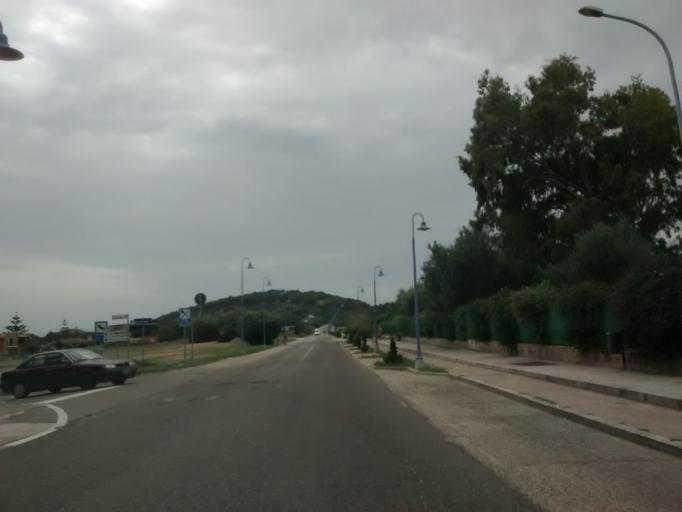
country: IT
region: Sardinia
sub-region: Provincia di Cagliari
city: Villasimius
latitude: 39.1361
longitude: 9.5232
